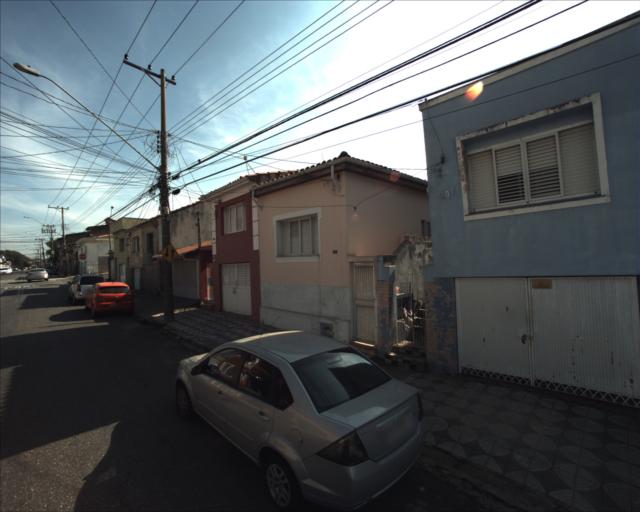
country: BR
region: Sao Paulo
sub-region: Sorocaba
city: Sorocaba
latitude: -23.4898
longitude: -47.4546
